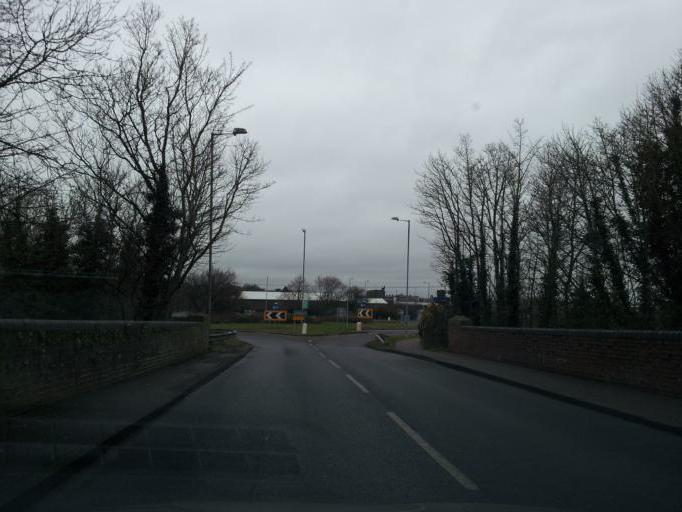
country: GB
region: England
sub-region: Essex
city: Dovercourt
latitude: 51.9386
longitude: 1.2568
